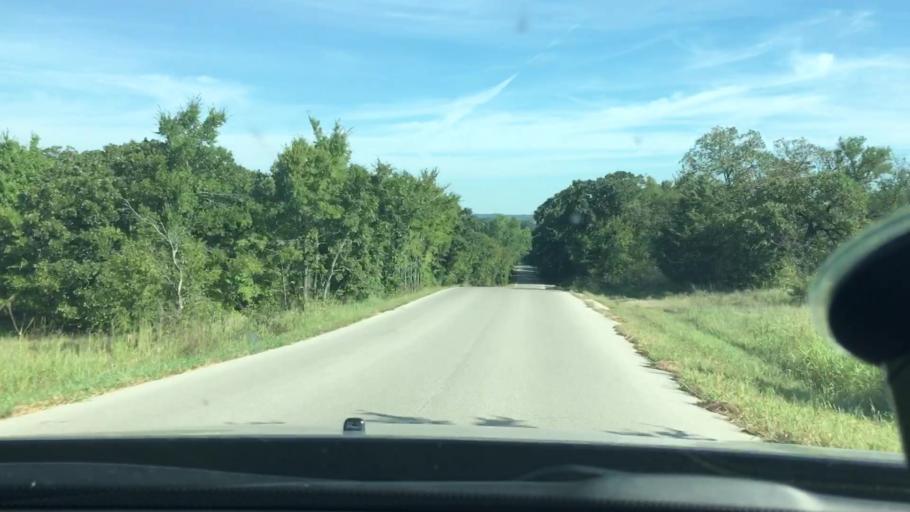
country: US
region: Oklahoma
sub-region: Carter County
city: Lone Grove
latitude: 34.2776
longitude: -97.2824
